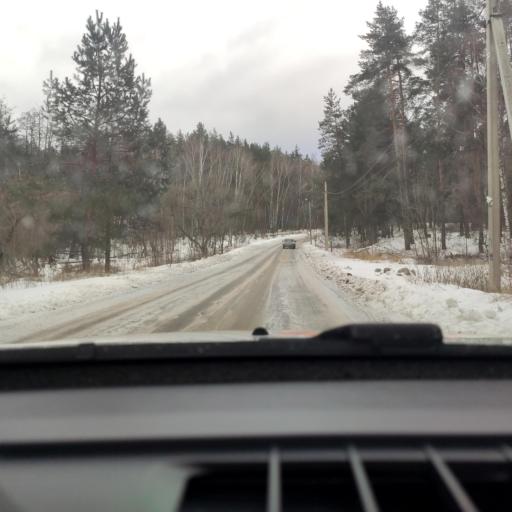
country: RU
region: Voronezj
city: Podgornoye
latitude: 51.7519
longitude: 39.1557
